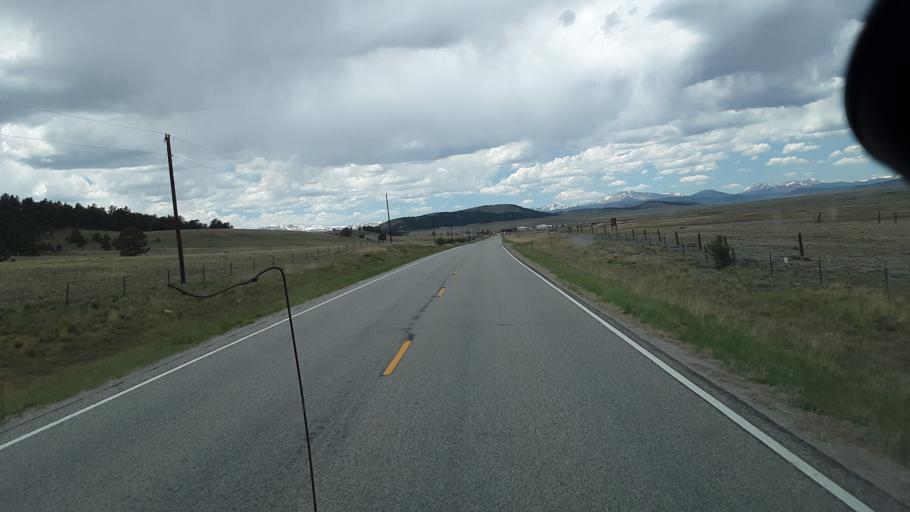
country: US
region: Colorado
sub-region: Park County
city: Fairplay
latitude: 39.0107
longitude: -105.7832
